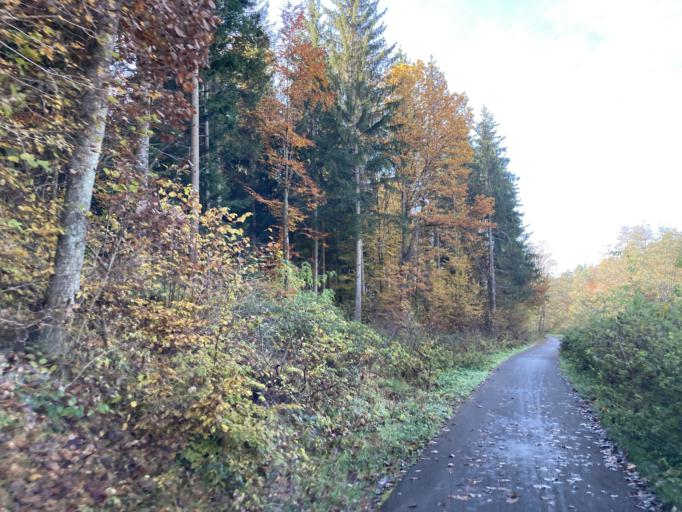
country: DE
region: Baden-Wuerttemberg
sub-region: Tuebingen Region
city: Bodelshausen
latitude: 48.4072
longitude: 8.9492
